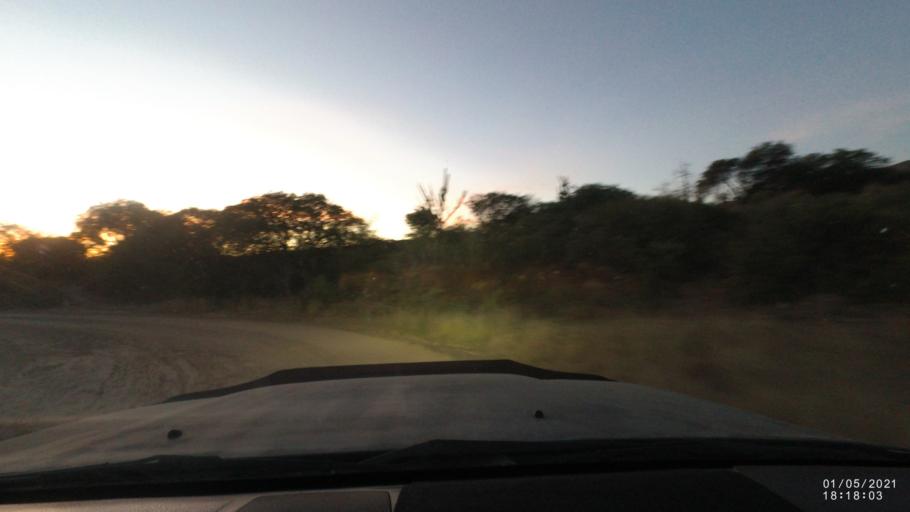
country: BO
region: Cochabamba
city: Capinota
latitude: -17.6651
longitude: -66.2190
